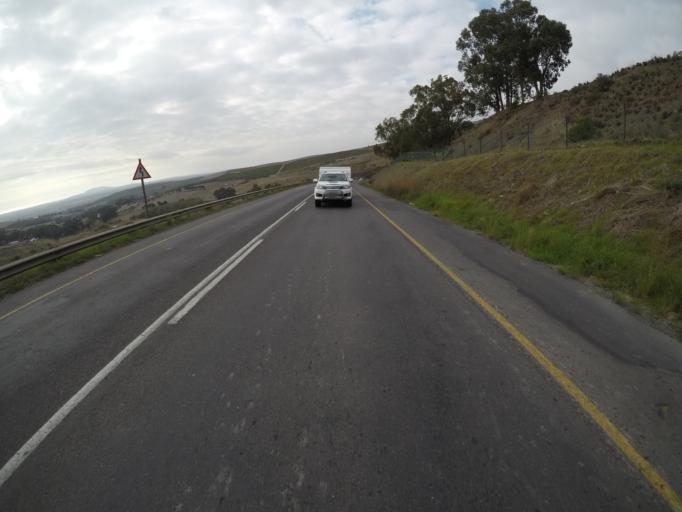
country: ZA
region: Western Cape
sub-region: City of Cape Town
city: Sunset Beach
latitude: -33.8292
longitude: 18.5891
